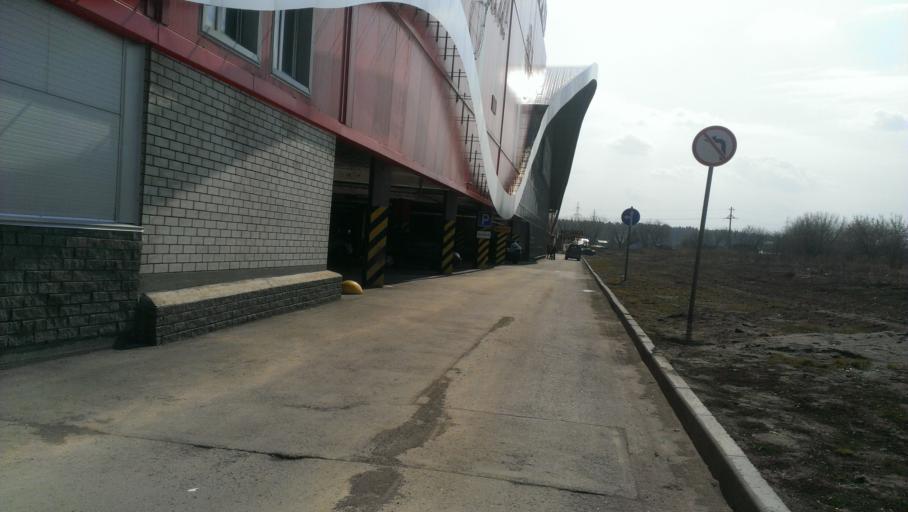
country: RU
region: Altai Krai
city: Novosilikatnyy
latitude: 53.3267
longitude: 83.6896
